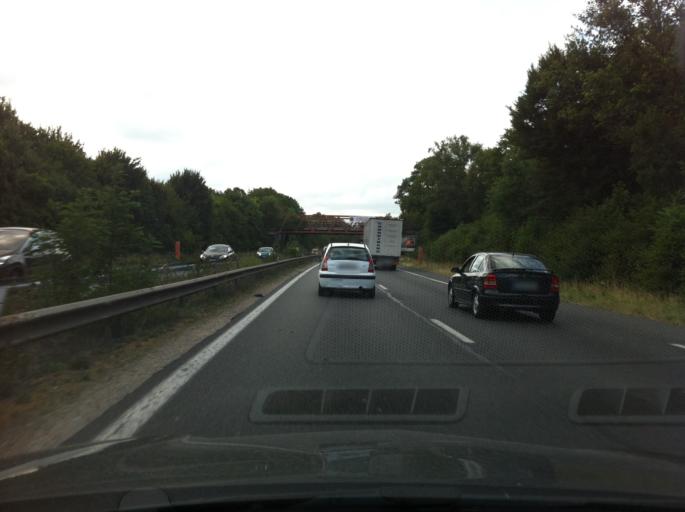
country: FR
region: Ile-de-France
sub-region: Departement de Seine-et-Marne
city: Lesigny
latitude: 48.7670
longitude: 2.6137
